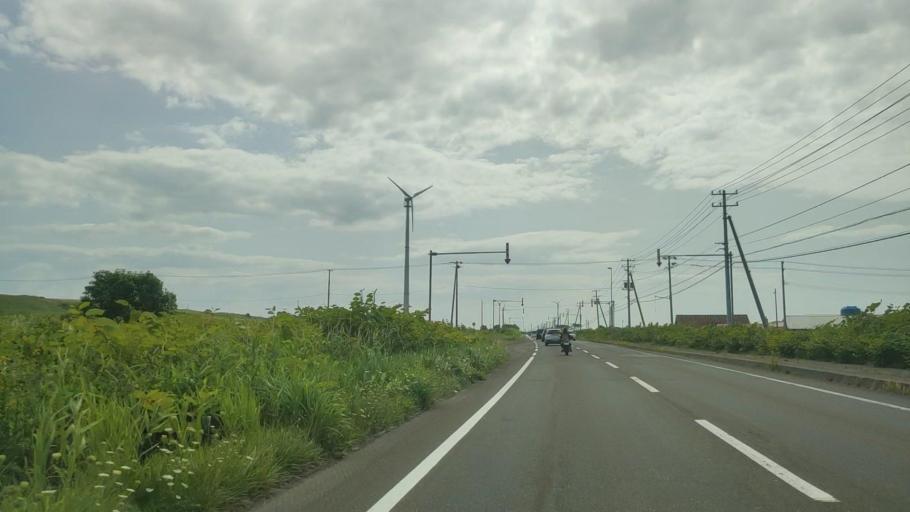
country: JP
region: Hokkaido
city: Rumoi
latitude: 44.3962
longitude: 141.7194
